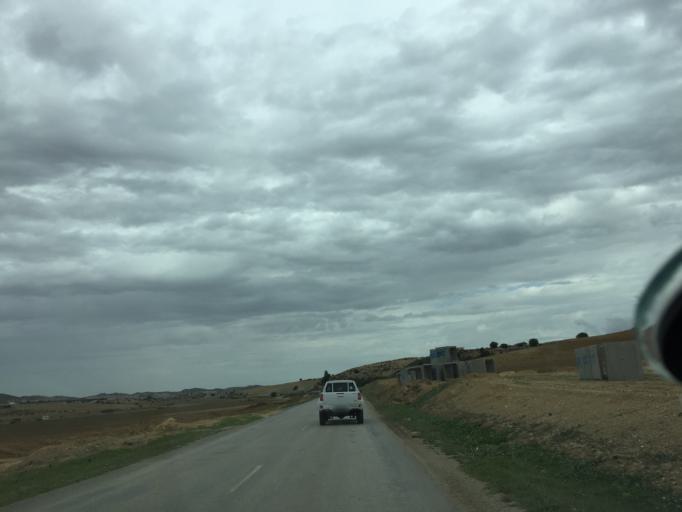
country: TN
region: Silyanah
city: Bu `Aradah
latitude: 36.2087
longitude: 9.7306
